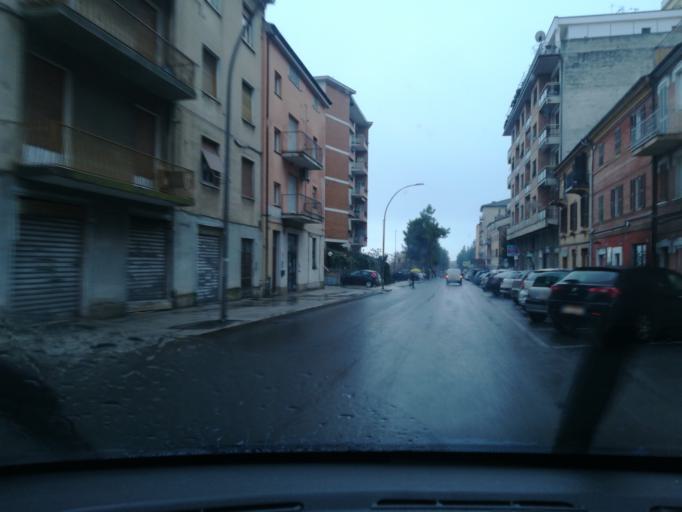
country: IT
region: The Marches
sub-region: Provincia di Macerata
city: Macerata
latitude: 43.2990
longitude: 13.4389
